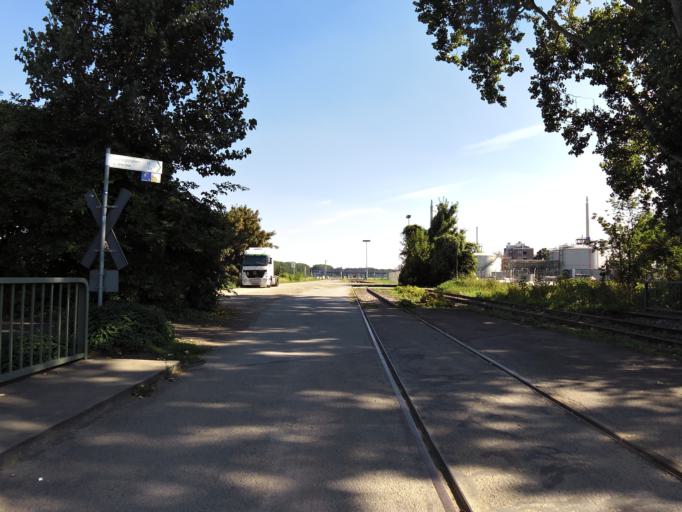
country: DE
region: Rheinland-Pfalz
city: Worms
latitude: 49.6605
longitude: 8.3659
